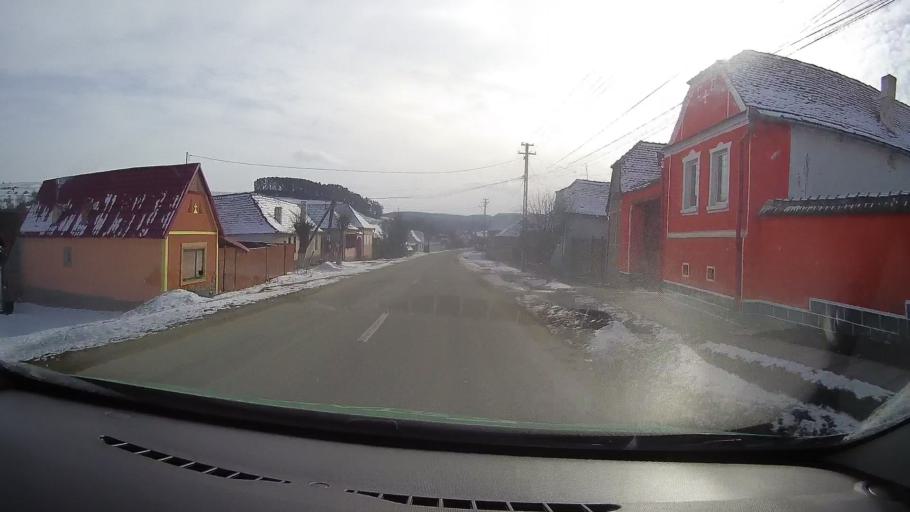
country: RO
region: Sibiu
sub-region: Comuna Bradeni
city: Bradeni
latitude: 46.0871
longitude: 24.8328
